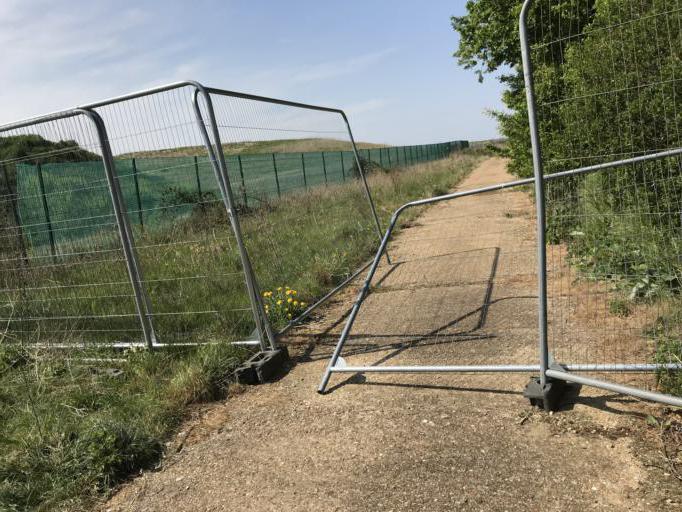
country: GB
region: England
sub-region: Cambridgeshire
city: Girton
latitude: 52.2250
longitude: 0.0859
